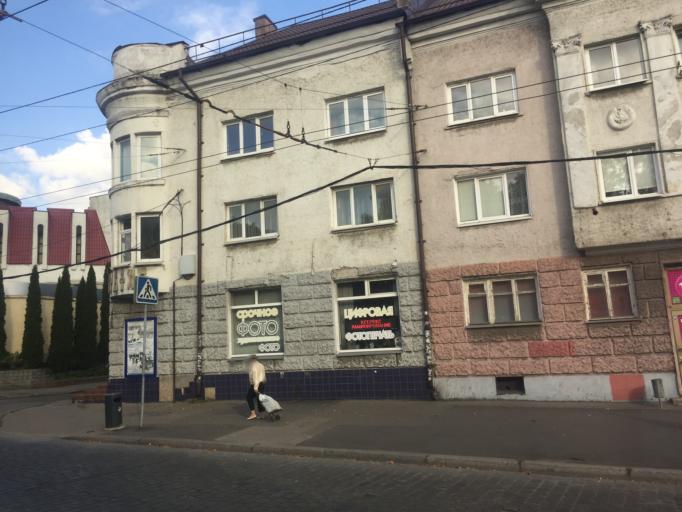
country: RU
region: Kaliningrad
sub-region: Gorod Kaliningrad
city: Kaliningrad
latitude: 54.6957
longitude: 20.5031
